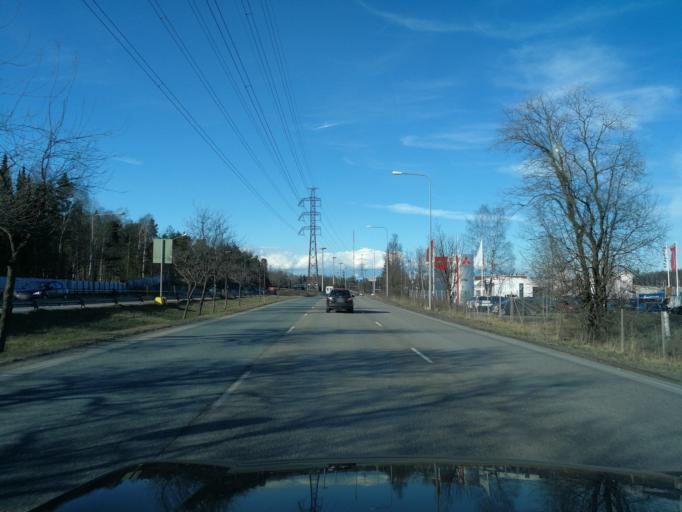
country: FI
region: Uusimaa
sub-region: Helsinki
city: Vantaa
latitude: 60.2017
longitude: 25.0401
